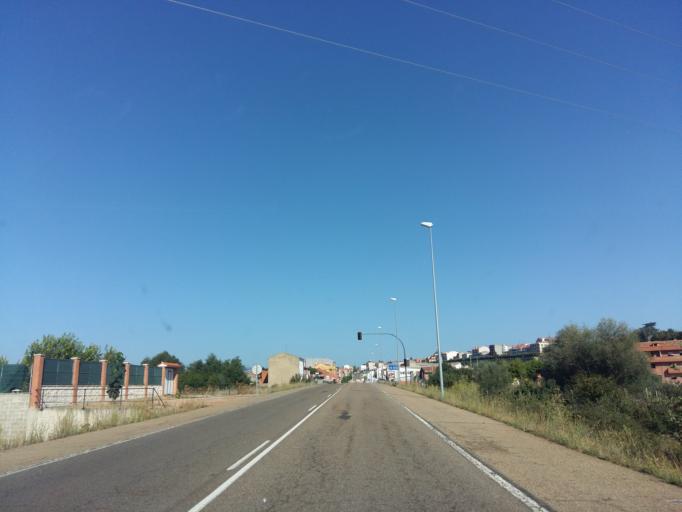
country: ES
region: Castille and Leon
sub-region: Provincia de Leon
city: Astorga
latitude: 42.4489
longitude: -6.0506
